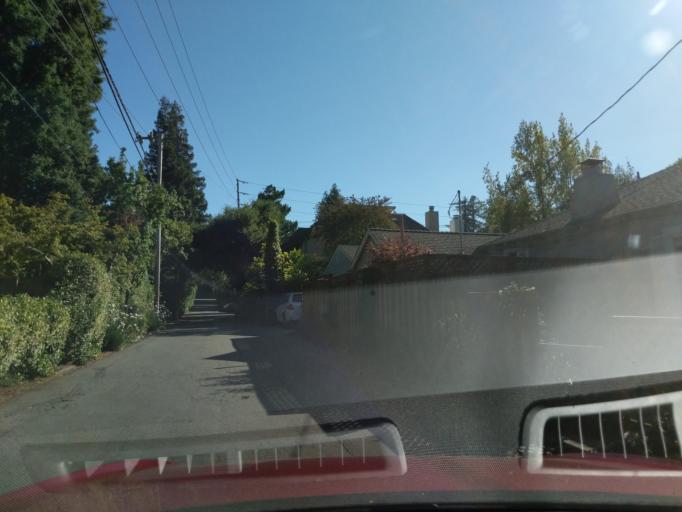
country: US
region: California
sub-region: San Mateo County
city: West Menlo Park
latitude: 37.4282
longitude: -122.1929
